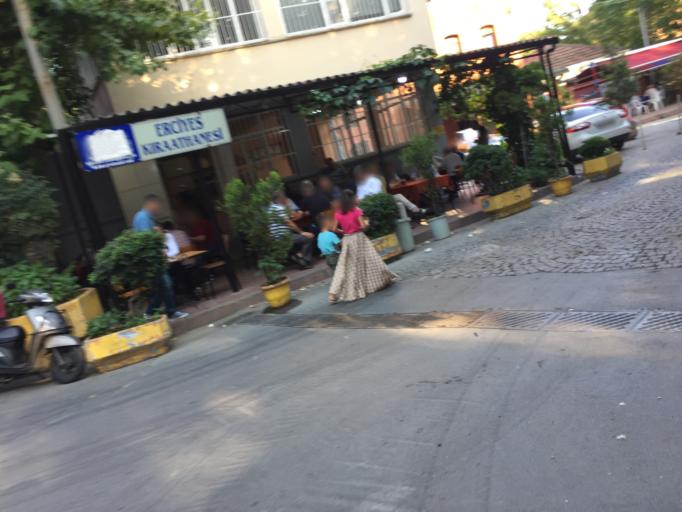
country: TR
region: Istanbul
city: Eminoenue
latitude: 41.0051
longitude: 28.9697
